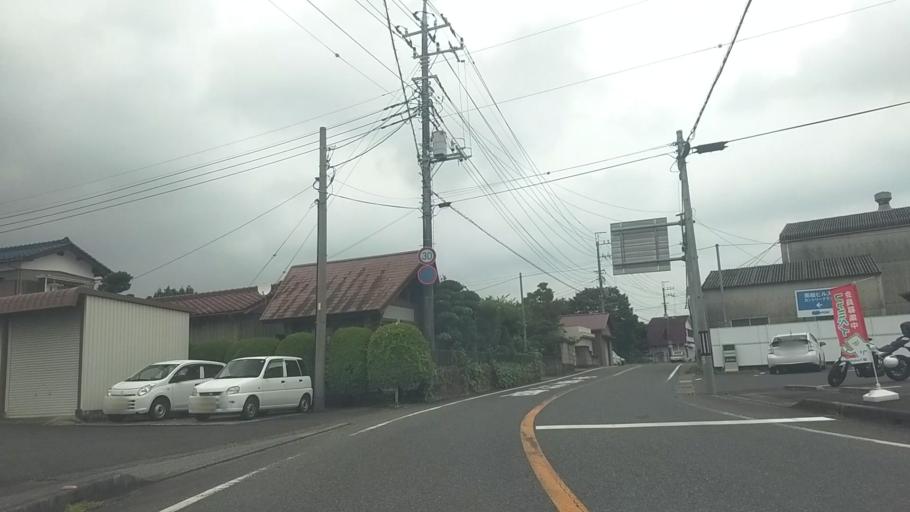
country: JP
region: Chiba
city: Kimitsu
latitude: 35.2157
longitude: 139.9271
